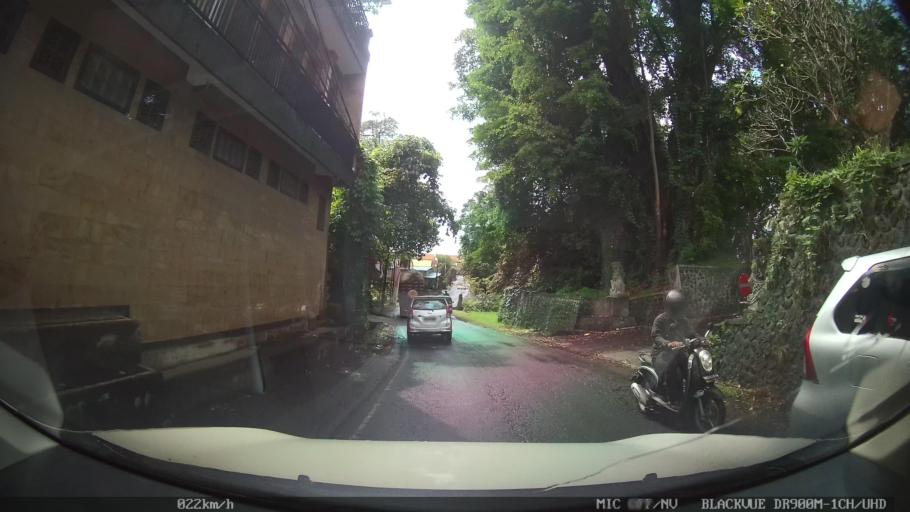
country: ID
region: Bali
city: Banjar Tebongkang
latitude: -8.5417
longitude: 115.2670
